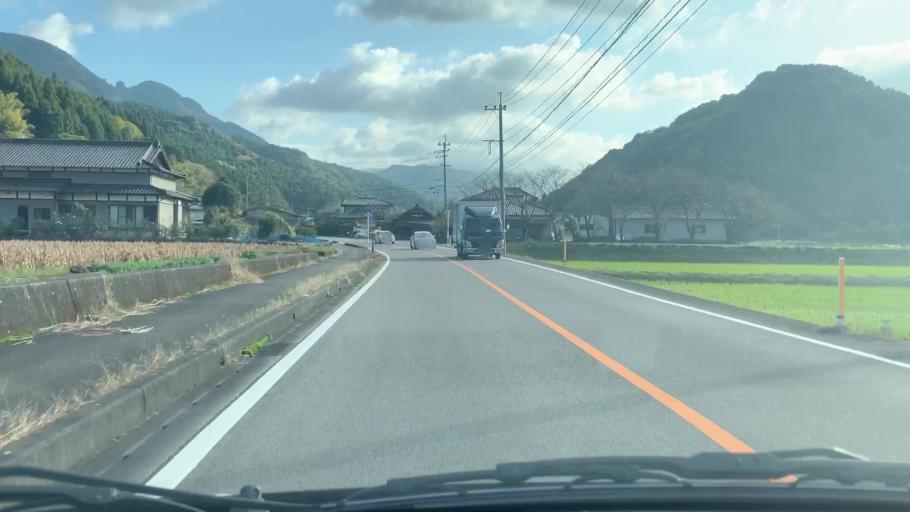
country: JP
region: Saga Prefecture
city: Kashima
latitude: 33.0735
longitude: 130.0683
